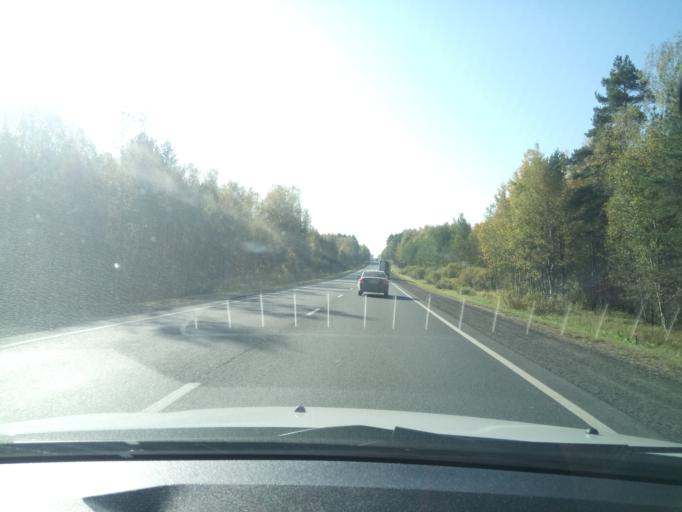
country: RU
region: Nizjnij Novgorod
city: Dal'neye Konstantinovo
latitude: 55.9560
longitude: 43.9763
